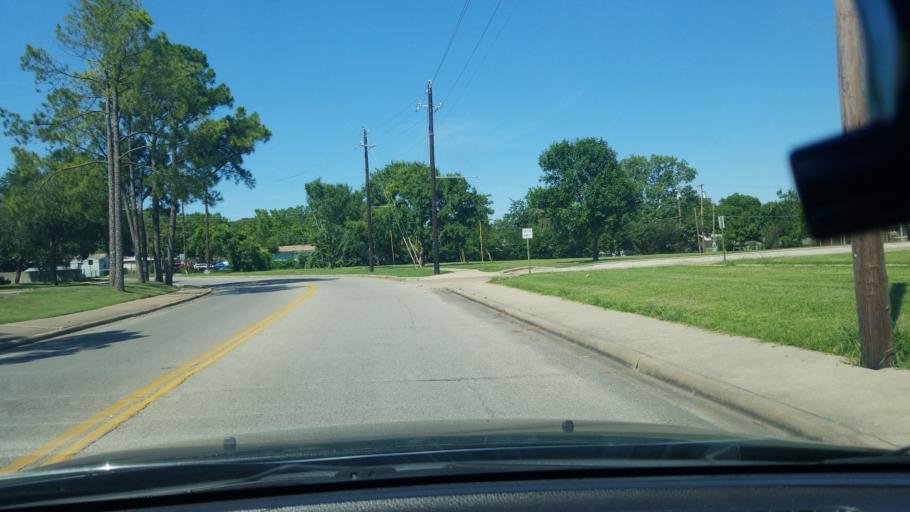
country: US
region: Texas
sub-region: Dallas County
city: Mesquite
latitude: 32.7790
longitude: -96.6148
